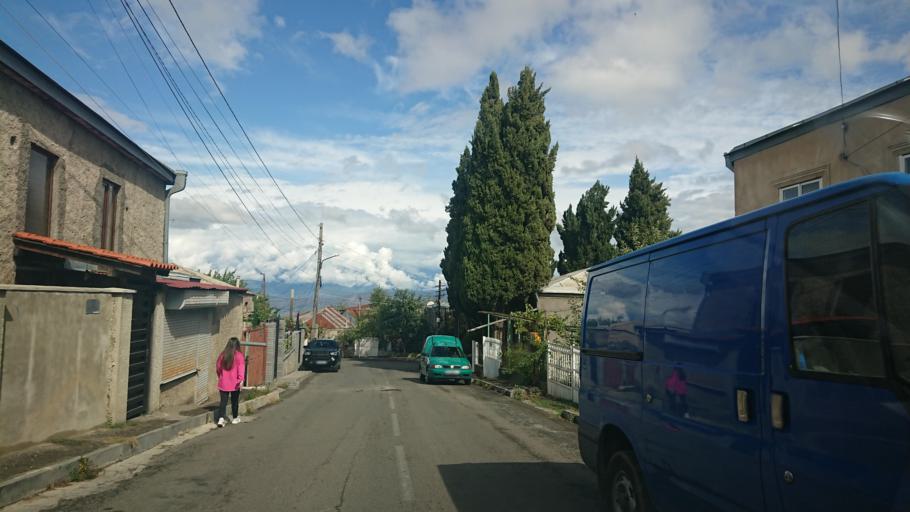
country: GE
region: Kakheti
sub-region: Telavi
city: Telavi
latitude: 41.9116
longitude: 45.4704
